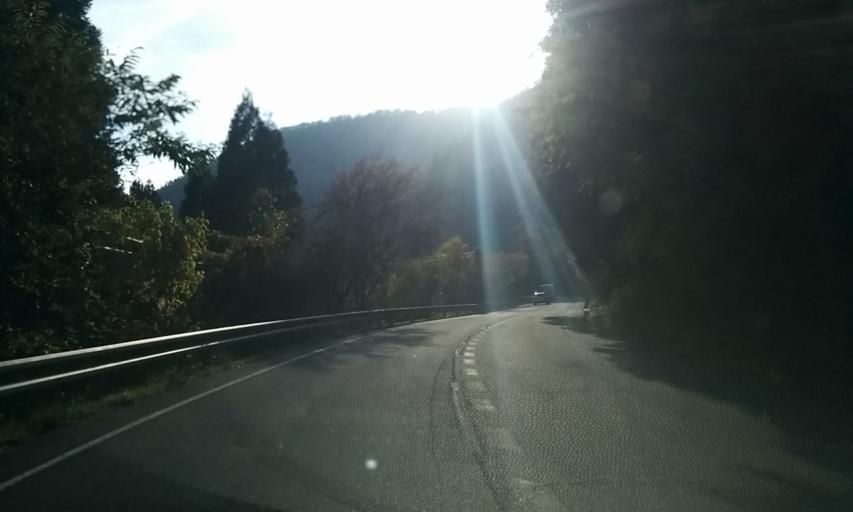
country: JP
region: Kyoto
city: Kameoka
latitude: 35.2487
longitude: 135.5609
